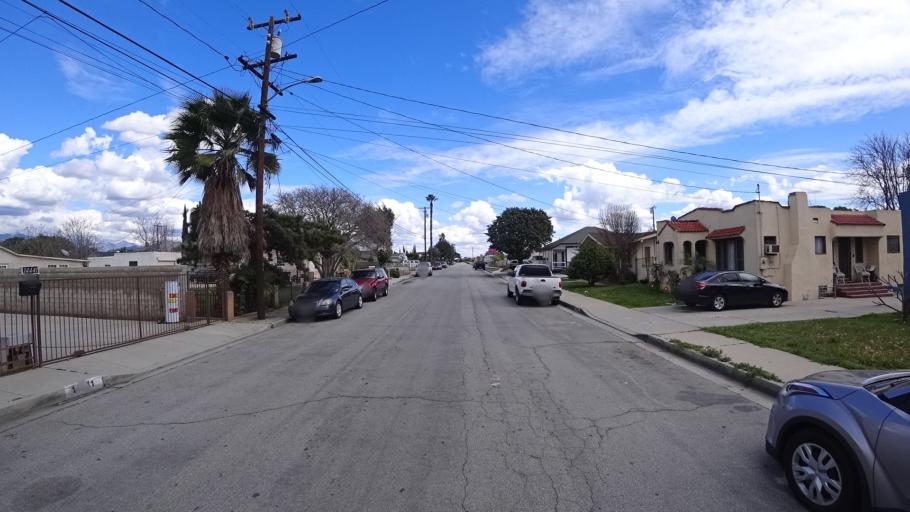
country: US
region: California
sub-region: Los Angeles County
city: Baldwin Park
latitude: 34.0978
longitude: -117.9594
